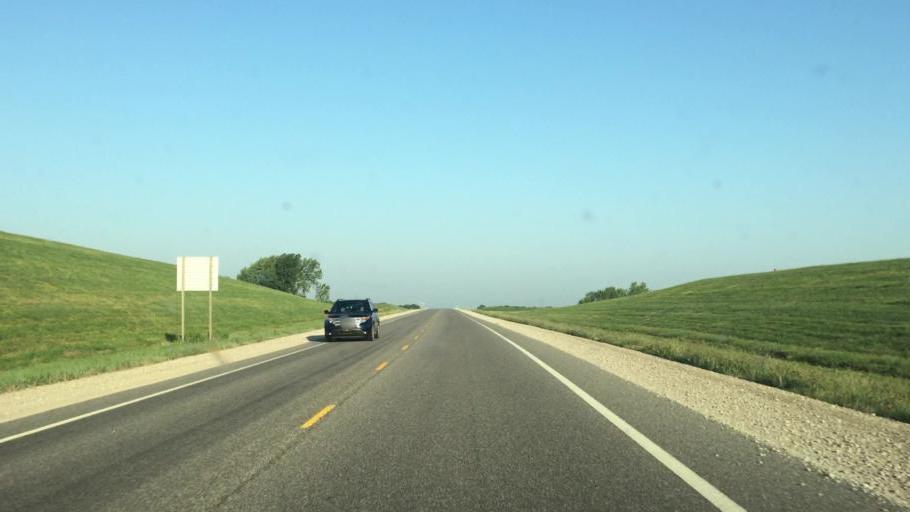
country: US
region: Kansas
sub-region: Doniphan County
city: Troy
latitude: 39.7979
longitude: -95.1170
